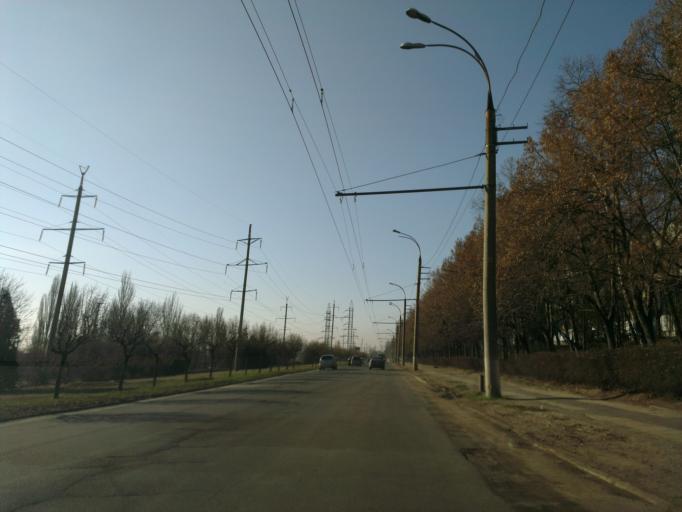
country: MD
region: Chisinau
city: Chisinau
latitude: 47.0235
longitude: 28.8878
